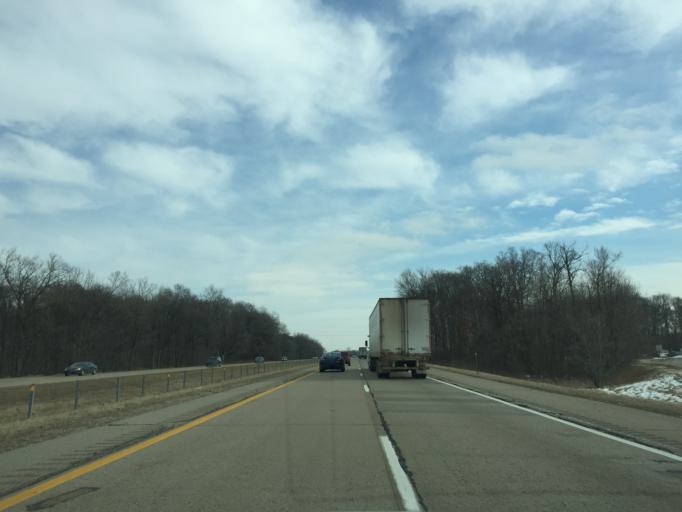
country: US
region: Michigan
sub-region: Ionia County
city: Saranac
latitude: 42.8792
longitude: -85.1632
